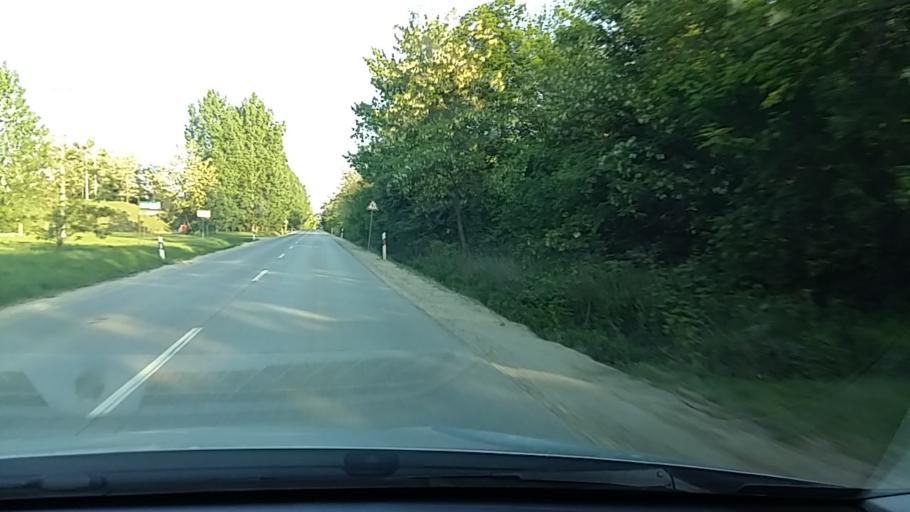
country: HU
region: Pest
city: Orbottyan
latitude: 47.6937
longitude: 19.2517
